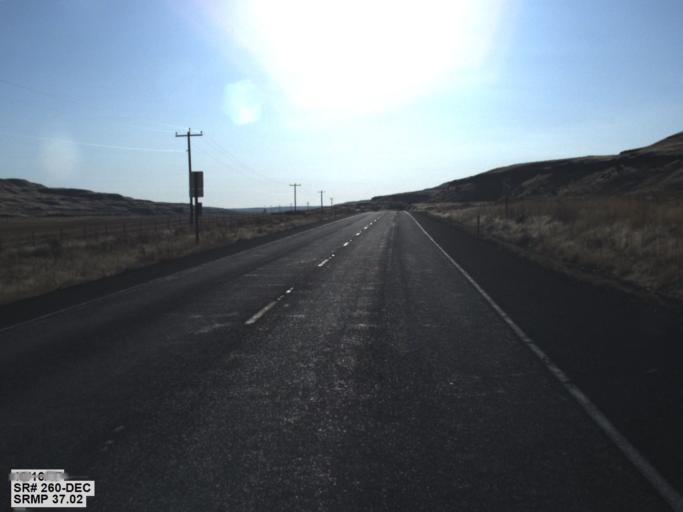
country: US
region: Washington
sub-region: Adams County
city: Ritzville
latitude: 46.7356
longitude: -118.3454
